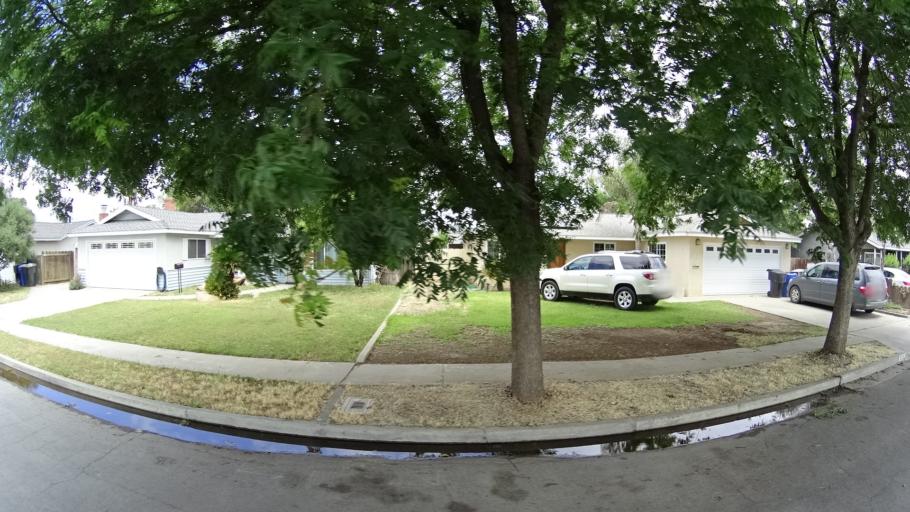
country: US
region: California
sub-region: Kings County
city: Hanford
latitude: 36.3413
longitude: -119.6272
